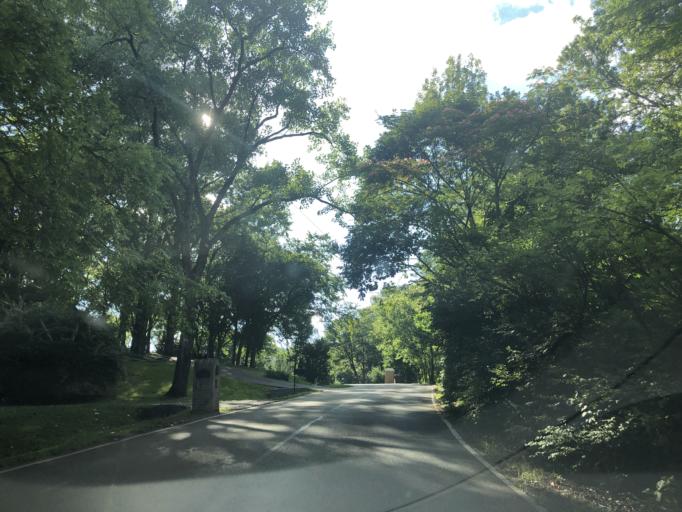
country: US
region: Tennessee
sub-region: Davidson County
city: Oak Hill
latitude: 36.0933
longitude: -86.8067
